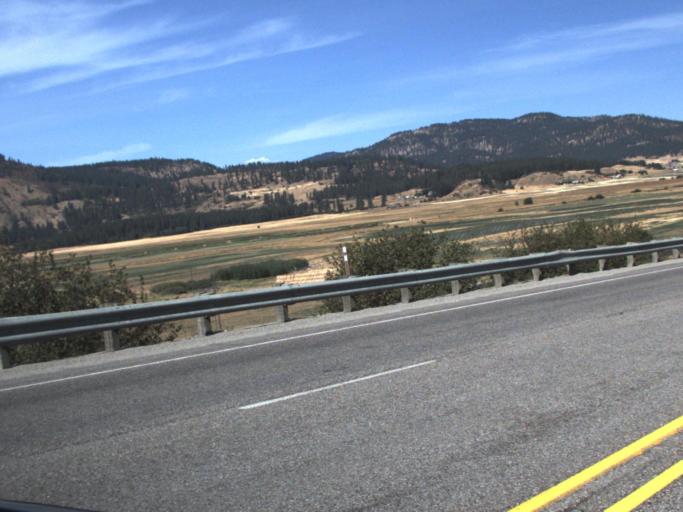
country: US
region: Washington
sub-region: Stevens County
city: Chewelah
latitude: 48.2064
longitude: -117.7151
